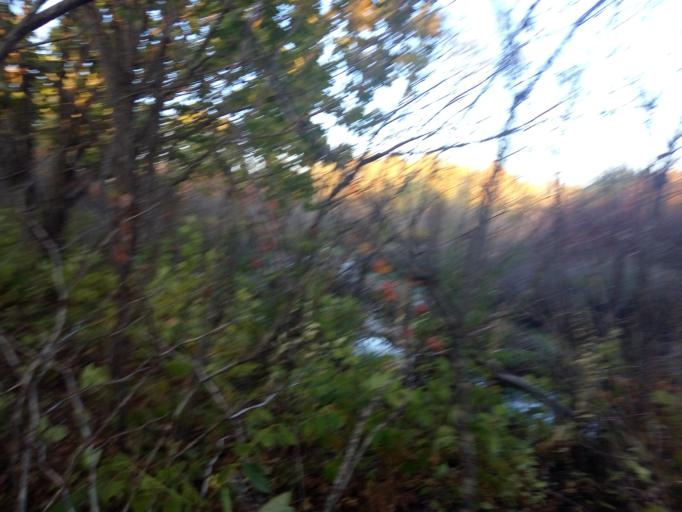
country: RU
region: Khabarovsk Krai
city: Khor
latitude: 47.7046
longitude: 134.9654
